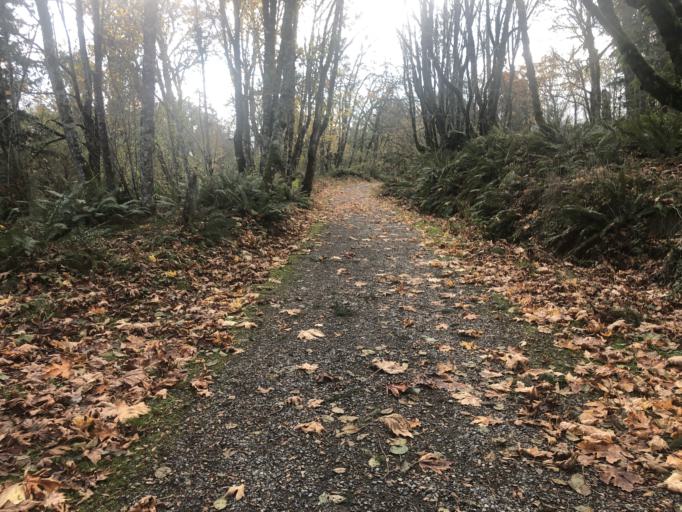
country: US
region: Washington
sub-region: Thurston County
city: Tanglewilde-Thompson Place
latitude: 47.1139
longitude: -122.7553
